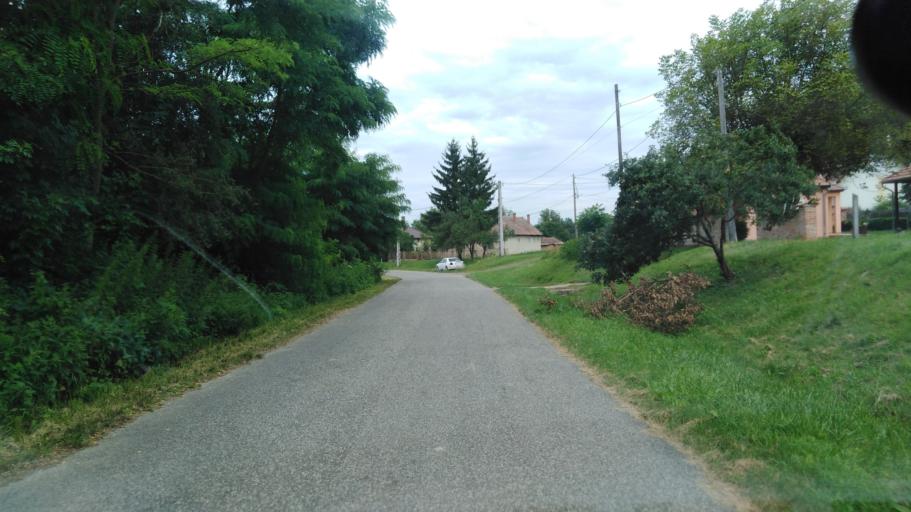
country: HU
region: Nograd
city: Karancskeszi
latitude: 48.2336
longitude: 19.6356
